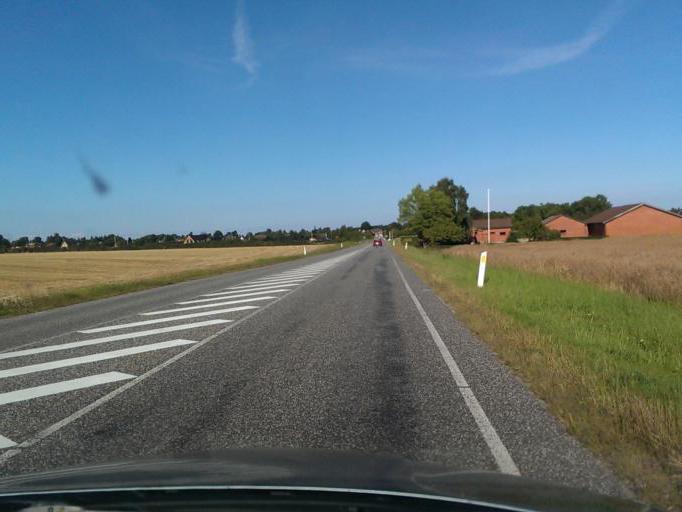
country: DK
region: Central Jutland
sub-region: Odder Kommune
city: Odder
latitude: 55.9214
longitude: 10.1431
